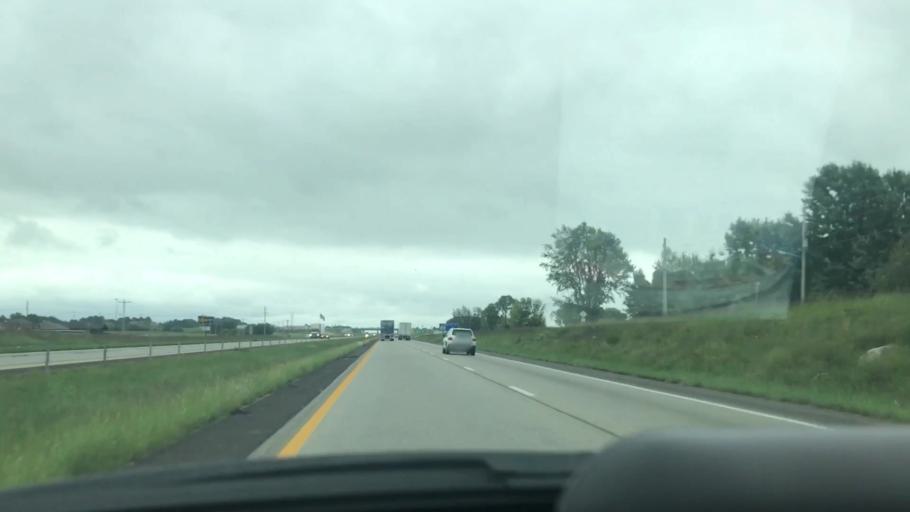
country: US
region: Missouri
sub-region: Greene County
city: Republic
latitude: 37.1986
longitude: -93.4319
